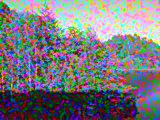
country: SE
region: Soedermanland
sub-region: Flens Kommun
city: Flen
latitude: 59.0678
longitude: 16.5911
